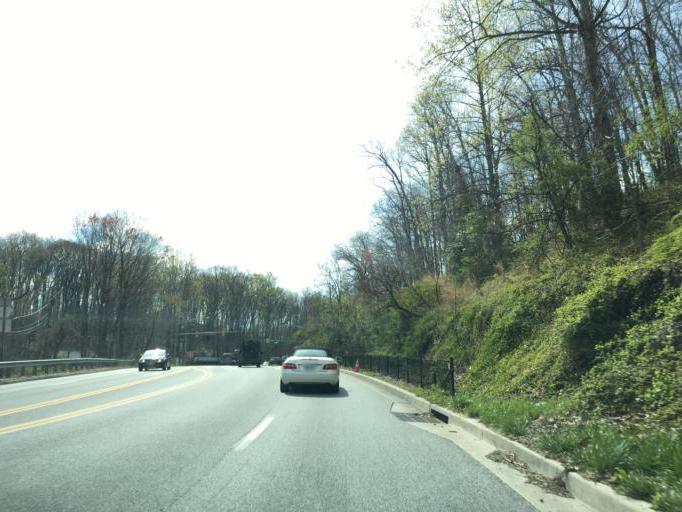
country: US
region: Maryland
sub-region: Baltimore County
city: Mays Chapel
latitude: 39.4534
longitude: -76.6519
